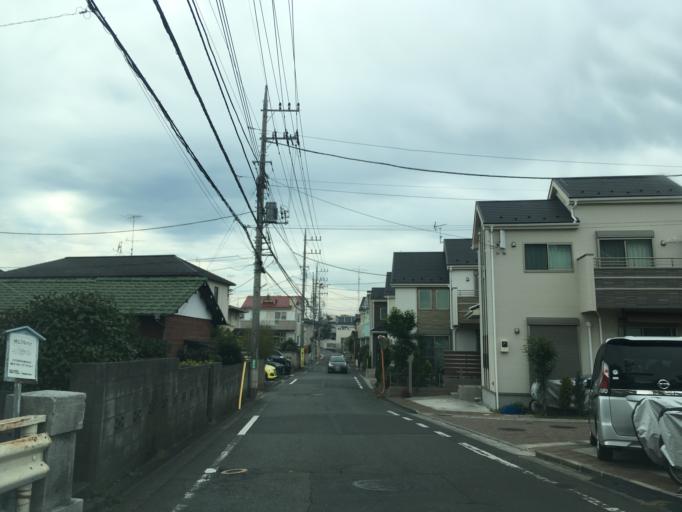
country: JP
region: Tokyo
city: Higashimurayama-shi
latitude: 35.7583
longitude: 139.4560
